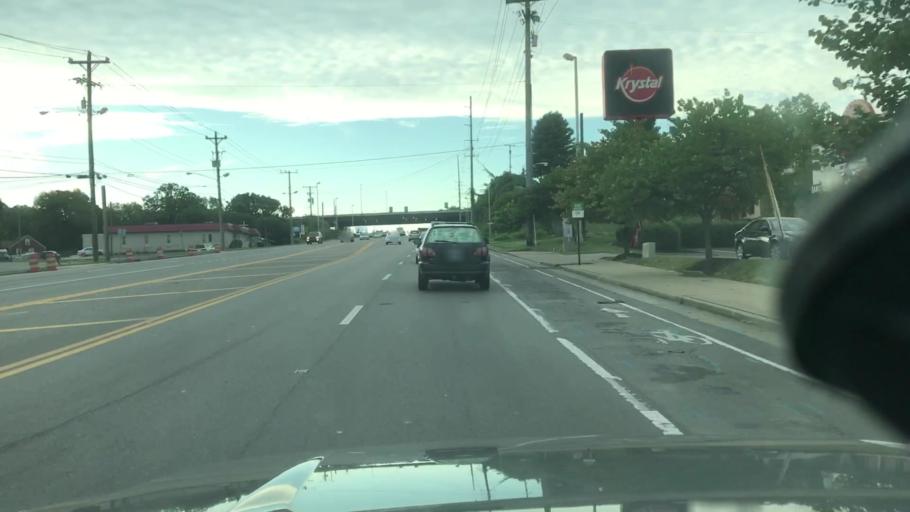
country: US
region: Tennessee
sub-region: Davidson County
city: Oak Hill
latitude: 36.1206
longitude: -86.7034
